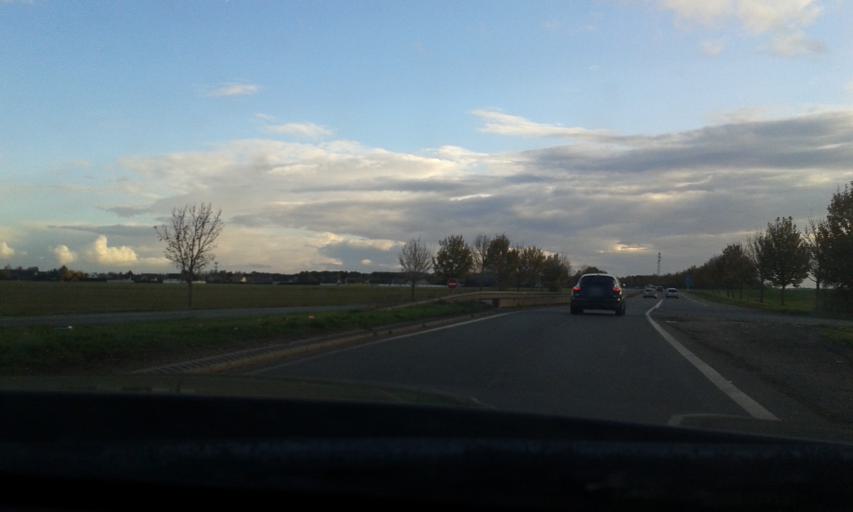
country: FR
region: Centre
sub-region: Departement d'Eure-et-Loir
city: Mainvilliers
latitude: 48.4363
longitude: 1.4309
